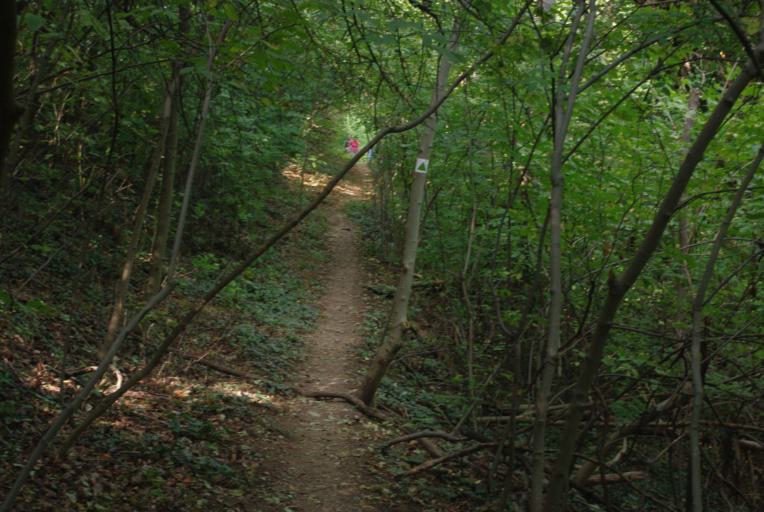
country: HU
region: Pest
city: Budaors
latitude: 47.4863
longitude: 18.9768
